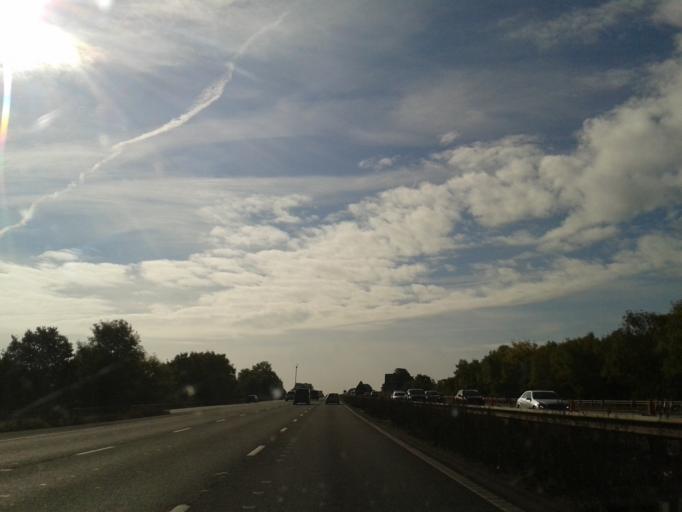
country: GB
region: England
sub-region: Staffordshire
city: Audley
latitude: 53.0642
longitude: -2.3321
